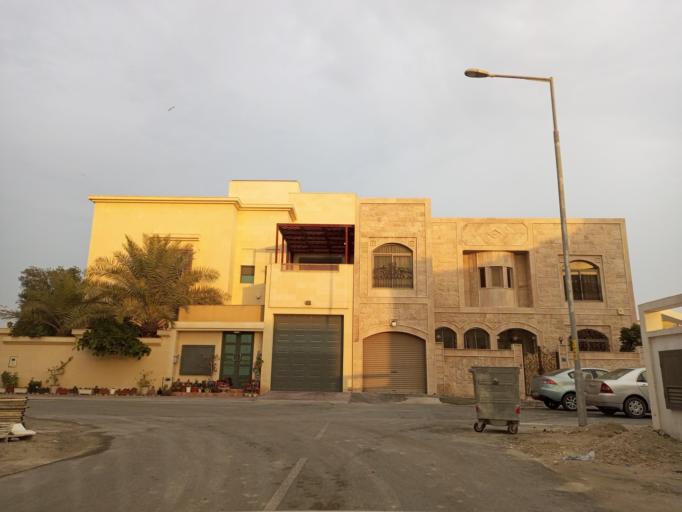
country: BH
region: Muharraq
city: Al Hadd
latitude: 26.2425
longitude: 50.6436
